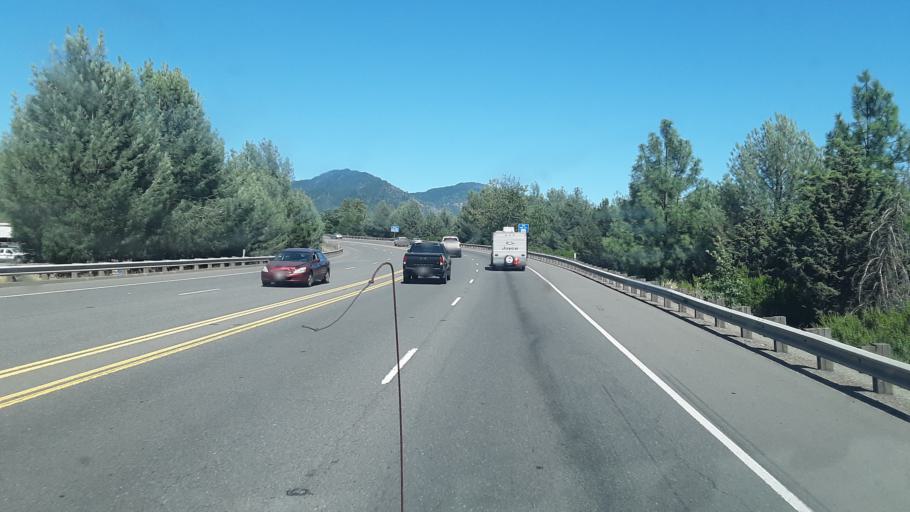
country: US
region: Oregon
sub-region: Josephine County
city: Fruitdale
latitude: 42.4327
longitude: -123.3155
